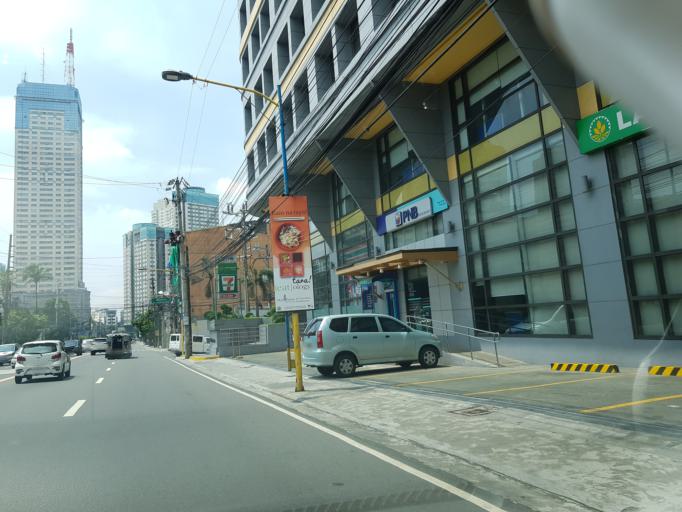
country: PH
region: Metro Manila
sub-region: Mandaluyong
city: Mandaluyong City
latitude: 14.5851
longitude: 121.0491
